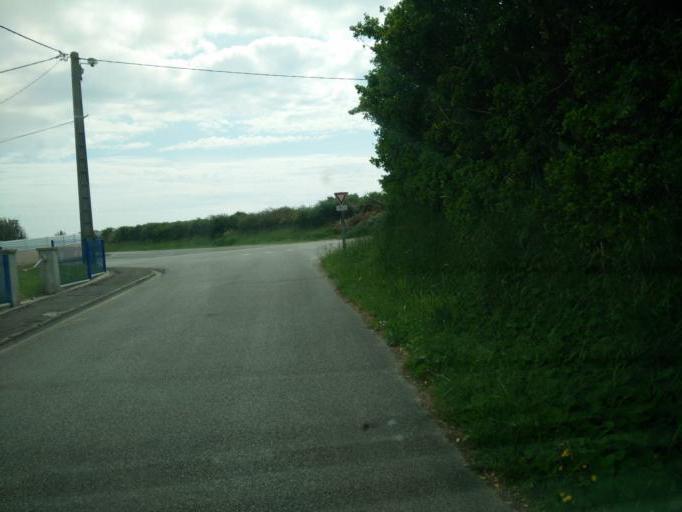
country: FR
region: Brittany
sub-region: Departement du Finistere
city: Camaret-sur-Mer
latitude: 48.2791
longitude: -4.6085
